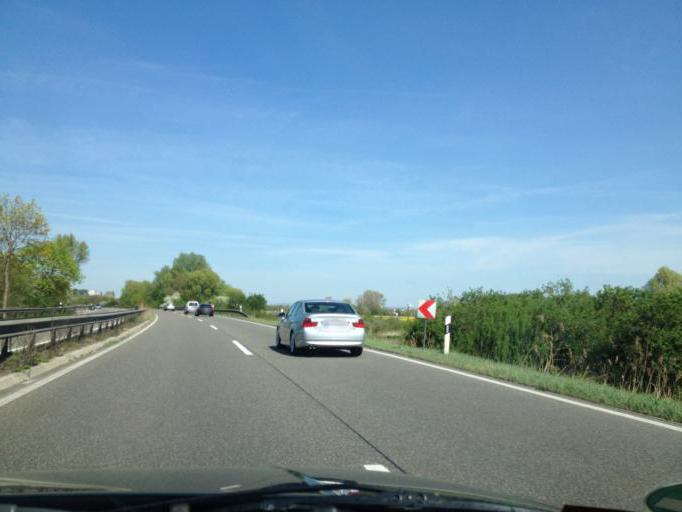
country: DE
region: Rheinland-Pfalz
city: Frankenthal
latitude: 49.5172
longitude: 8.3636
